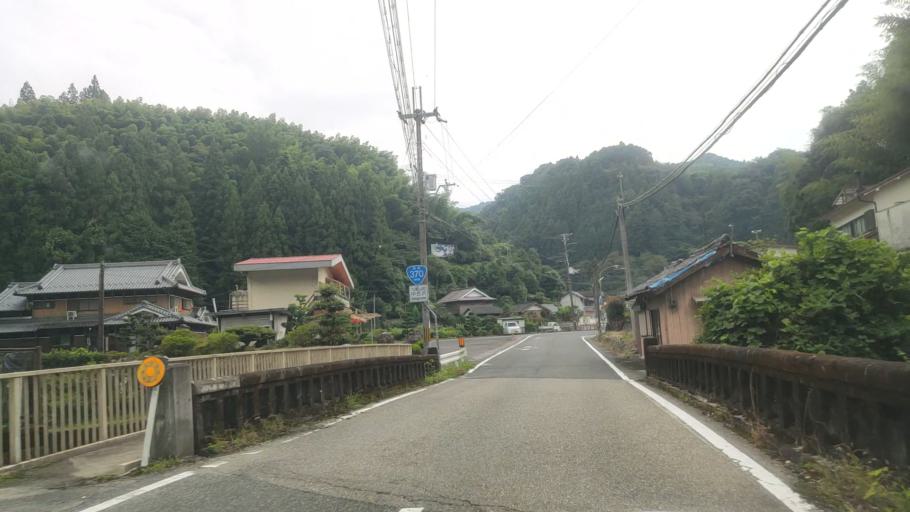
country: JP
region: Wakayama
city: Hashimoto
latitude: 34.2639
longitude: 135.5510
